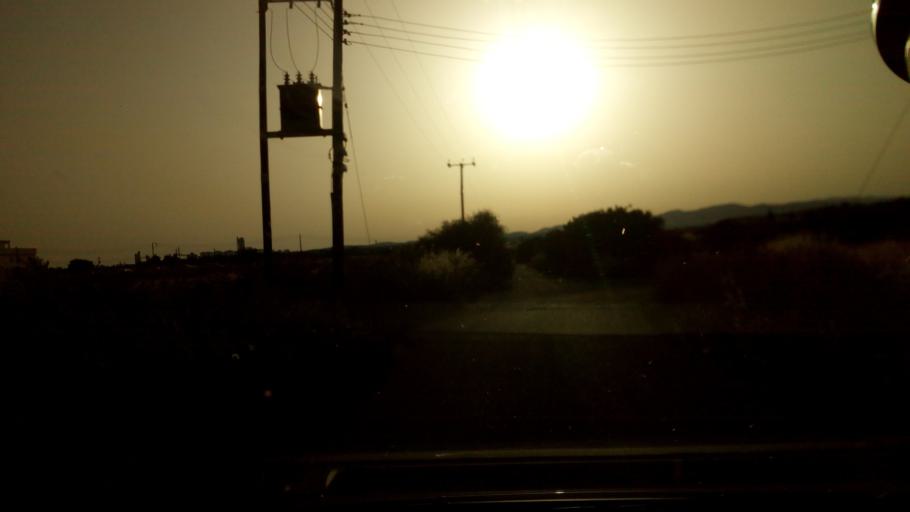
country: CY
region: Larnaka
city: Kofinou
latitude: 34.7358
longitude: 33.3508
